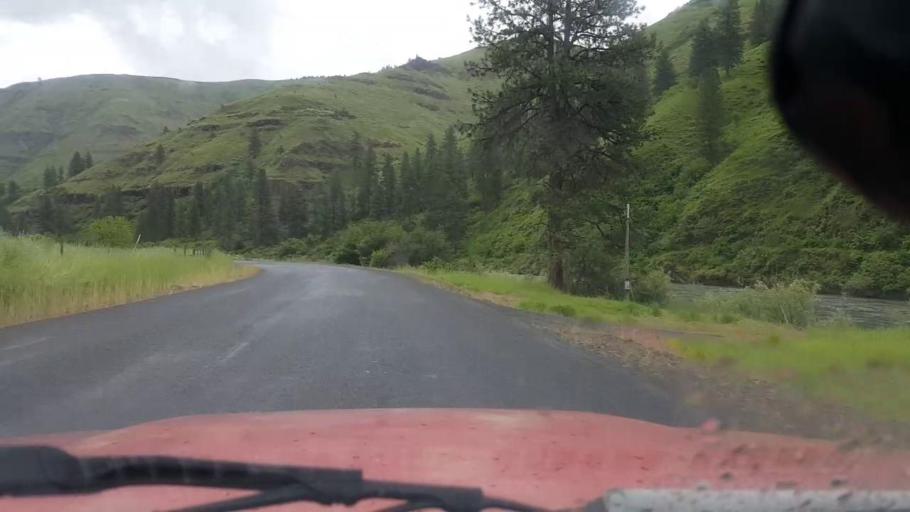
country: US
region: Washington
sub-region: Asotin County
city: Asotin
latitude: 46.0280
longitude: -117.3131
